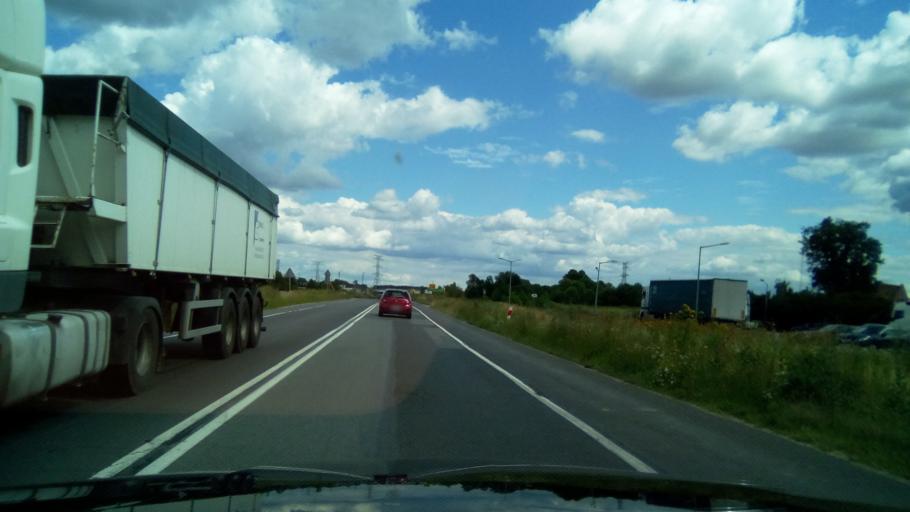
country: PL
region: Kujawsko-Pomorskie
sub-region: Powiat bydgoski
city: Biale Blota
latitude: 53.0800
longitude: 17.8615
